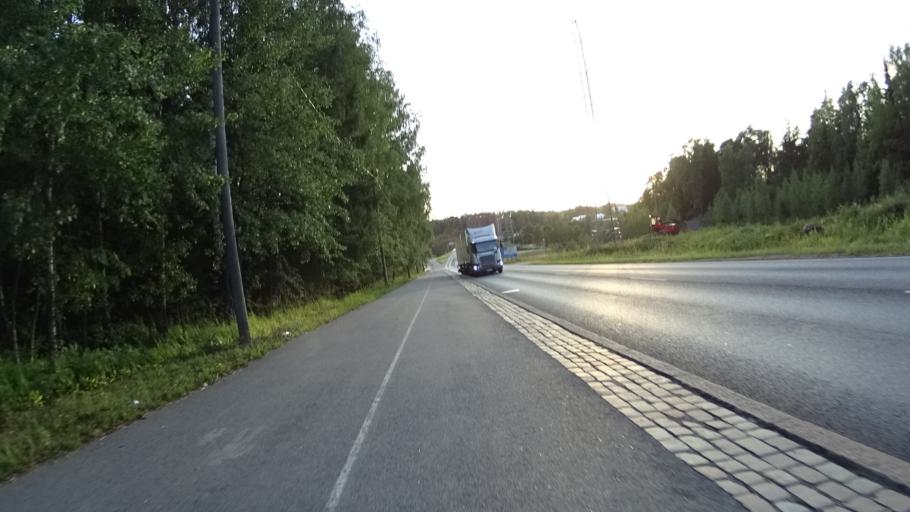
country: FI
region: Uusimaa
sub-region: Helsinki
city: Helsinki
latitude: 60.2200
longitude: 24.9184
